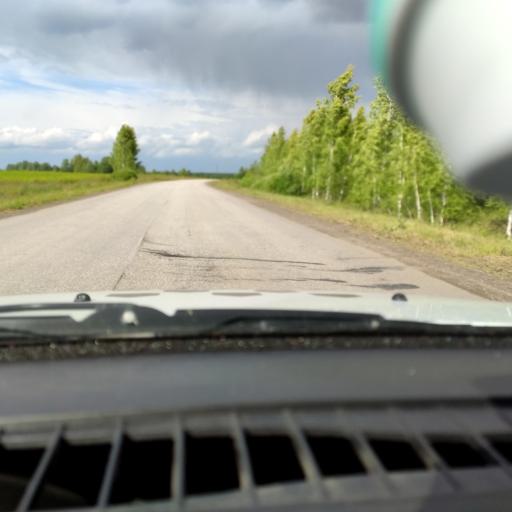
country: RU
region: Perm
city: Orda
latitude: 57.1868
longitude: 56.8487
